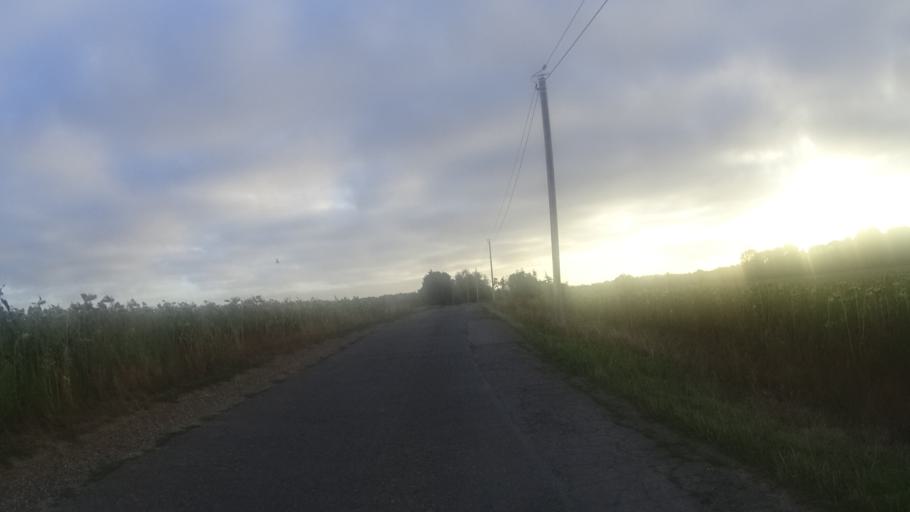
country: FR
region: Ile-de-France
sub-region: Departement de l'Essonne
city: Vert-le-Petit
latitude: 48.5588
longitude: 2.3760
